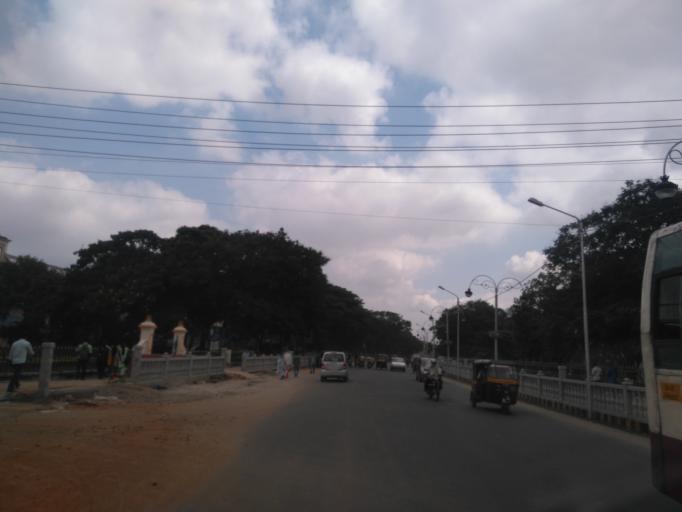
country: IN
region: Karnataka
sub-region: Mysore
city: Mysore
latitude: 12.3050
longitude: 76.6523
